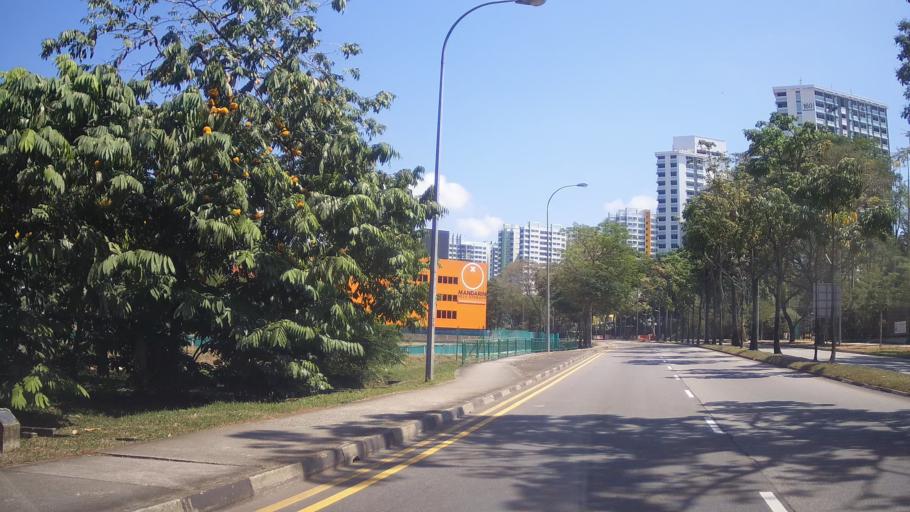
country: SG
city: Singapore
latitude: 1.3275
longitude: 103.7202
